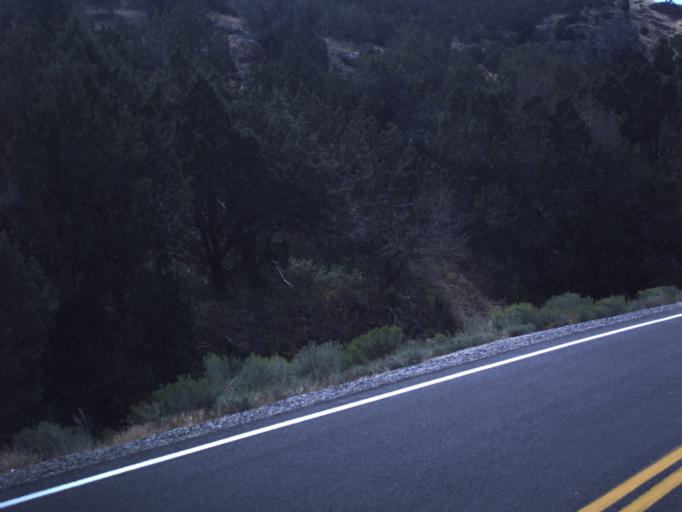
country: US
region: Utah
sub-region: Tooele County
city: Grantsville
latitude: 40.3452
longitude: -112.5861
